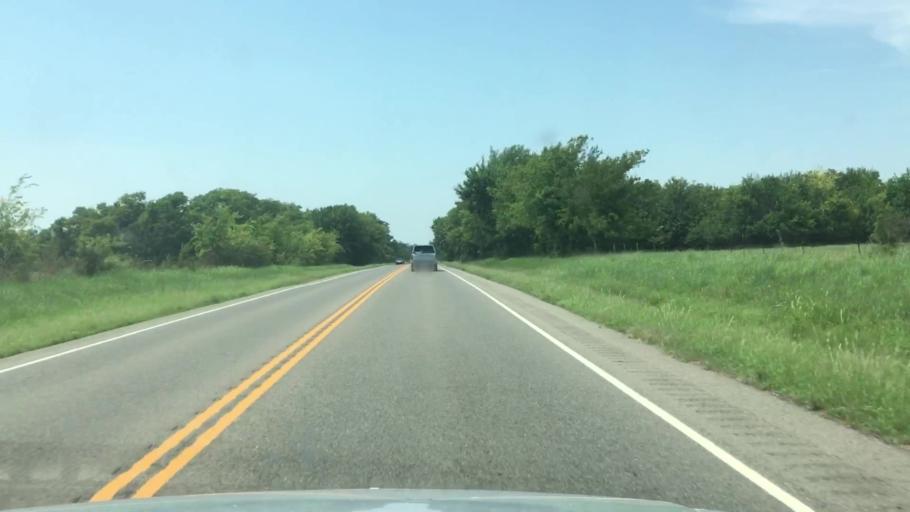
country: US
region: Oklahoma
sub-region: Wagoner County
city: Wagoner
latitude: 35.9389
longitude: -95.3072
